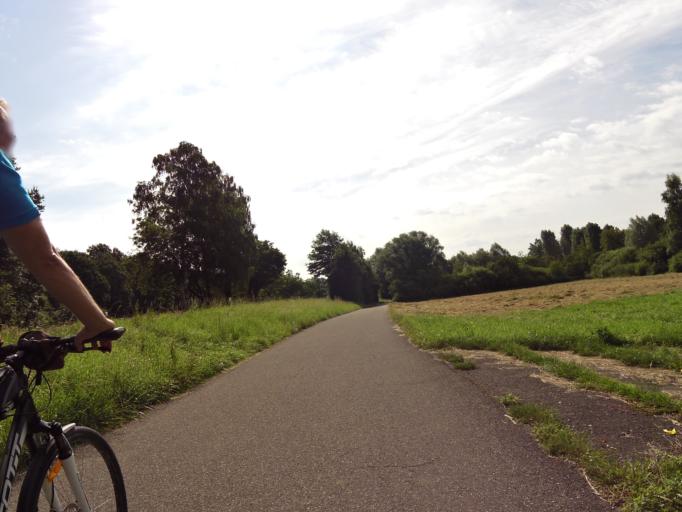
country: DE
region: Baden-Wuerttemberg
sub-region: Freiburg Region
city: Radolfzell am Bodensee
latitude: 47.7316
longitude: 9.0220
